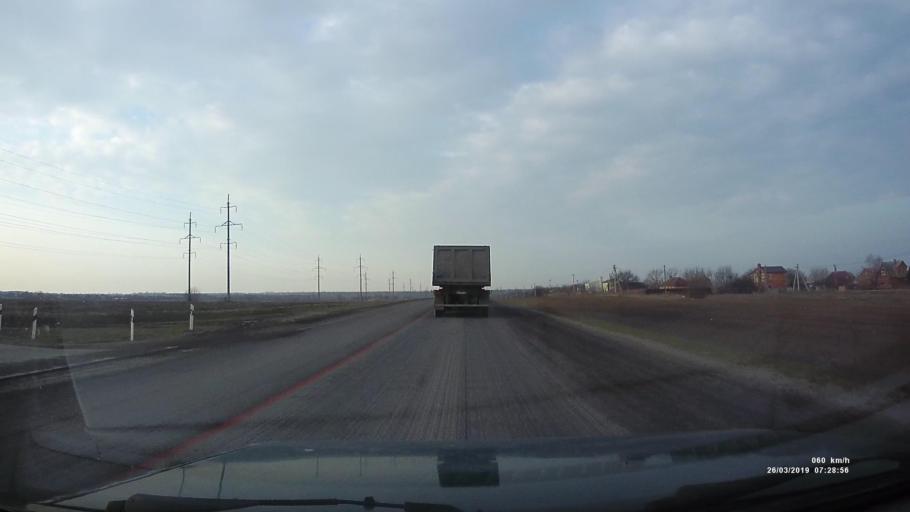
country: RU
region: Rostov
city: Novobessergenovka
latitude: 47.2496
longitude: 38.8204
